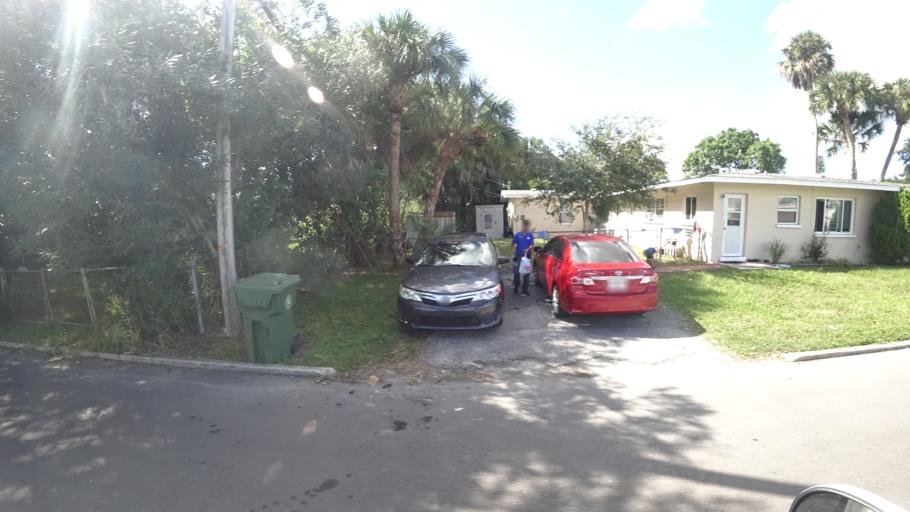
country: US
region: Florida
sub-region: Manatee County
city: South Bradenton
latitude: 27.4781
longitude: -82.5795
